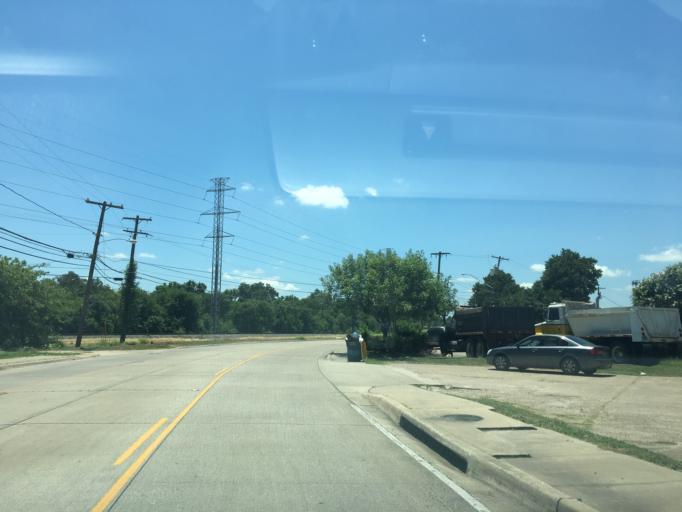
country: US
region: Texas
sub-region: Dallas County
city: Garland
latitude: 32.8472
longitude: -96.6832
